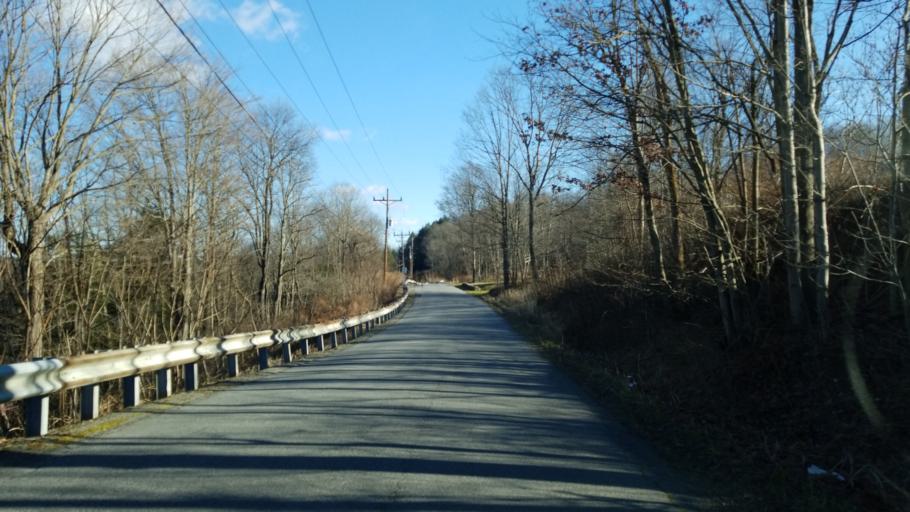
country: US
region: Pennsylvania
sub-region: Clearfield County
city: Hyde
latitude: 40.9846
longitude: -78.4800
